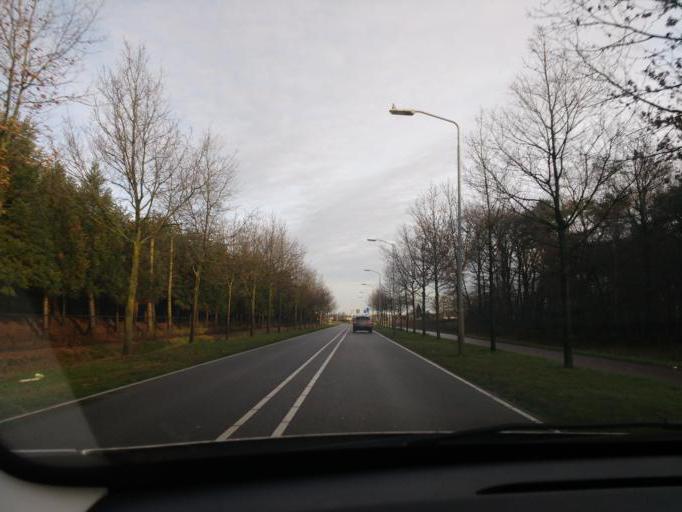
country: NL
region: North Brabant
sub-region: Gemeente Asten
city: Asten
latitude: 51.4471
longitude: 5.7748
